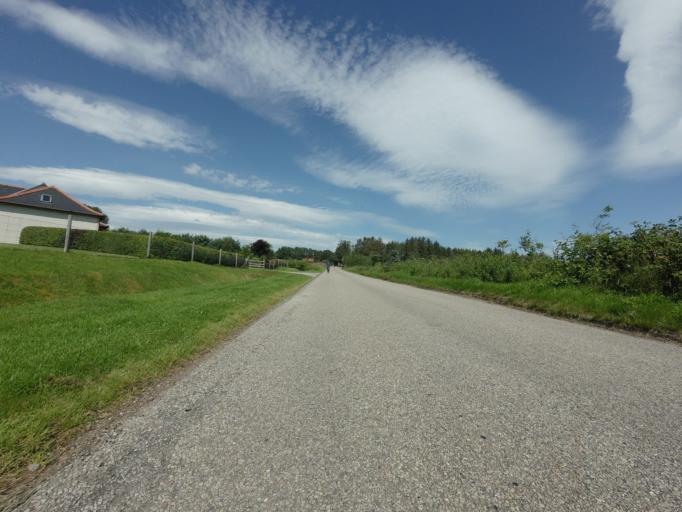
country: GB
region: Scotland
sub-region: Highland
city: Inverness
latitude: 57.5295
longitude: -4.3198
